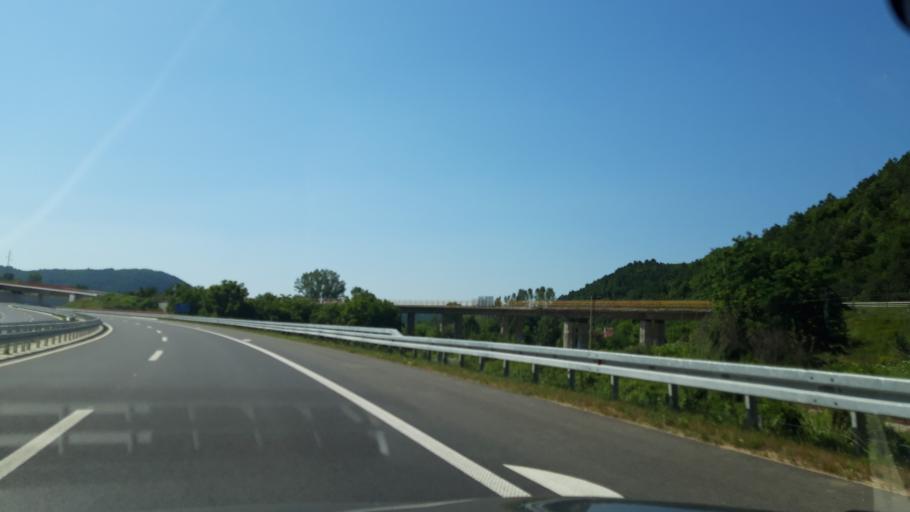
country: RS
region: Central Serbia
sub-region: Jablanicki Okrug
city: Vlasotince
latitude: 42.8750
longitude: 22.0882
